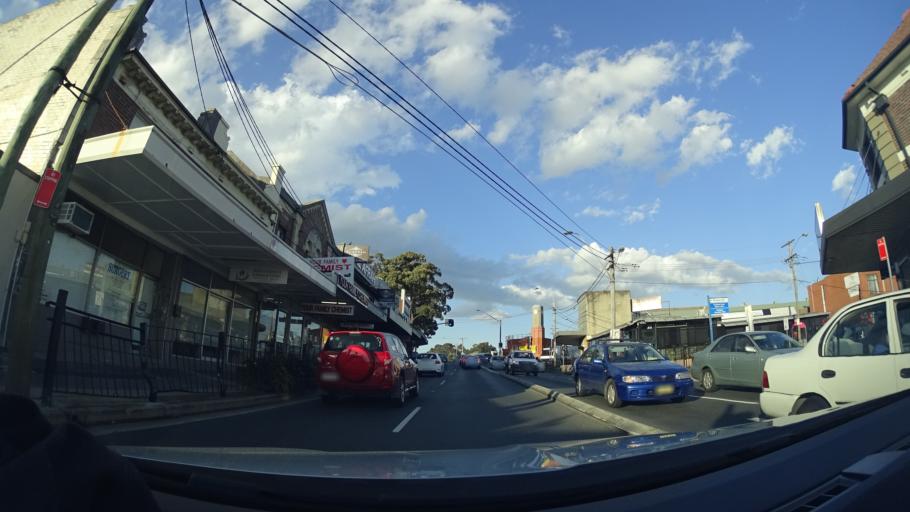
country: AU
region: New South Wales
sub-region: Canterbury
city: Roselands
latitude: -33.9260
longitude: 151.0540
